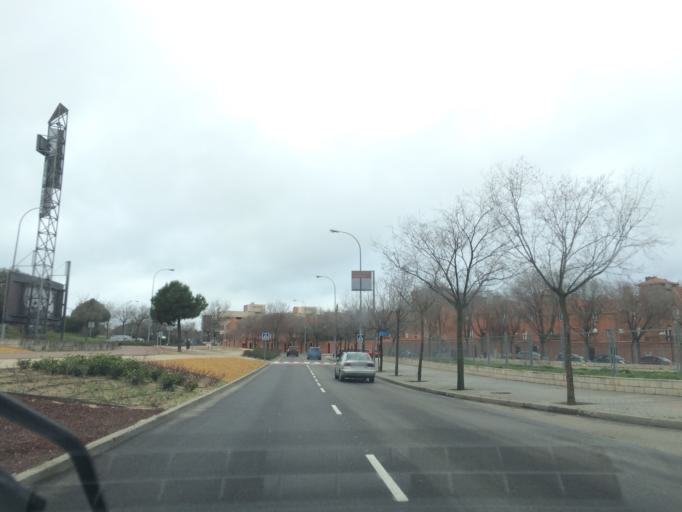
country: ES
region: Madrid
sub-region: Provincia de Madrid
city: Tres Cantos
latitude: 40.5925
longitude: -3.6975
